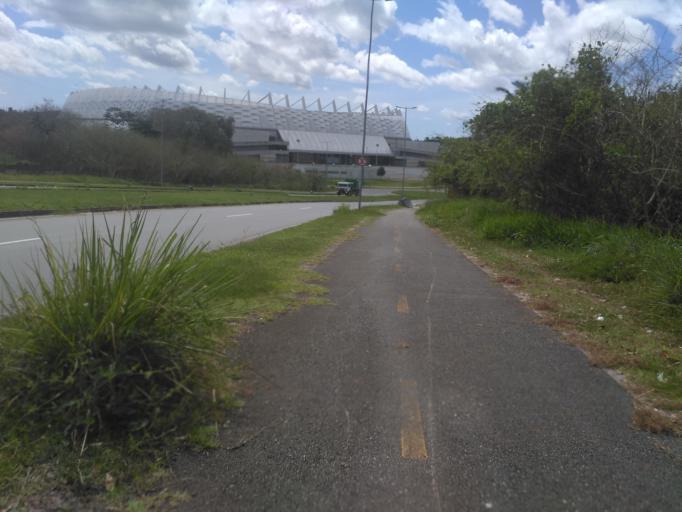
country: BR
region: Pernambuco
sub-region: Sao Lourenco Da Mata
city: Sao Lourenco da Mata
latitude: -8.0442
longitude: -35.0102
